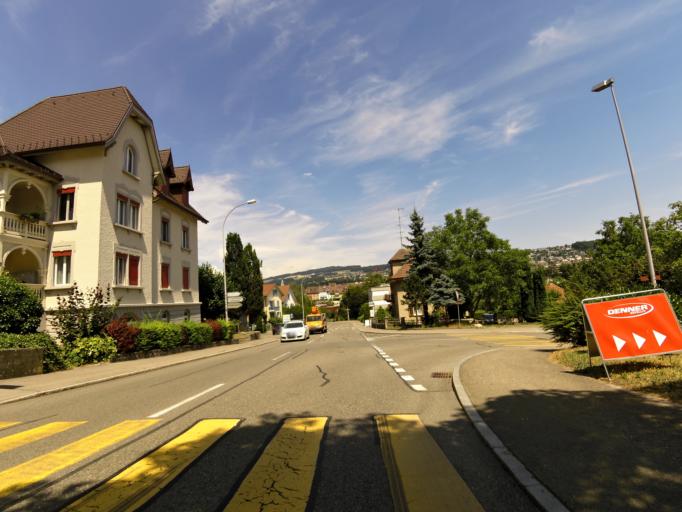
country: CH
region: Aargau
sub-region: Bezirk Bremgarten
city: Bremgarten
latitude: 47.3467
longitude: 8.3399
